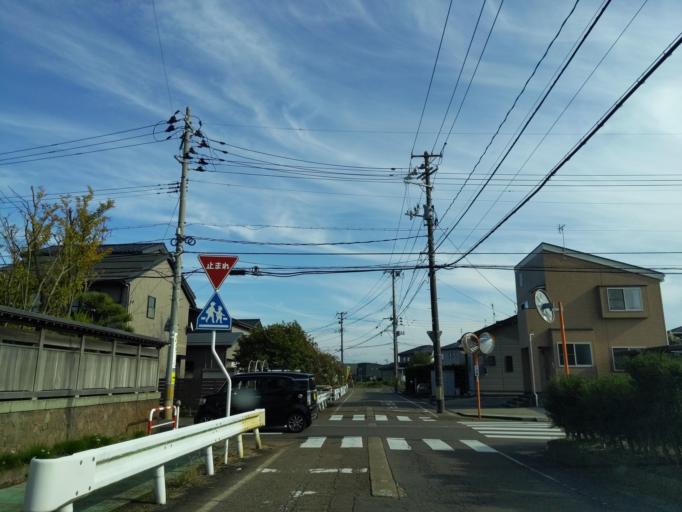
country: JP
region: Niigata
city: Sanjo
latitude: 37.6203
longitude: 138.9405
